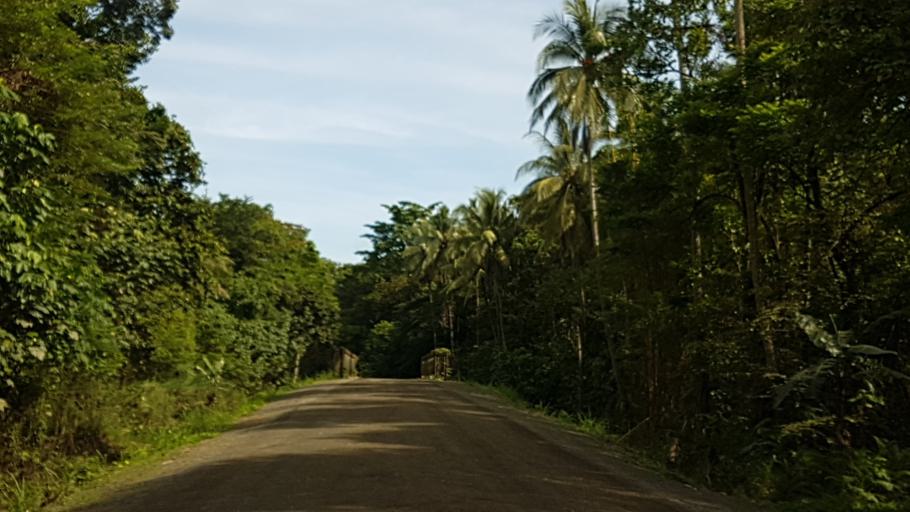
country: PG
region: Milne Bay
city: Alotau
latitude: -10.3388
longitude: 150.5496
